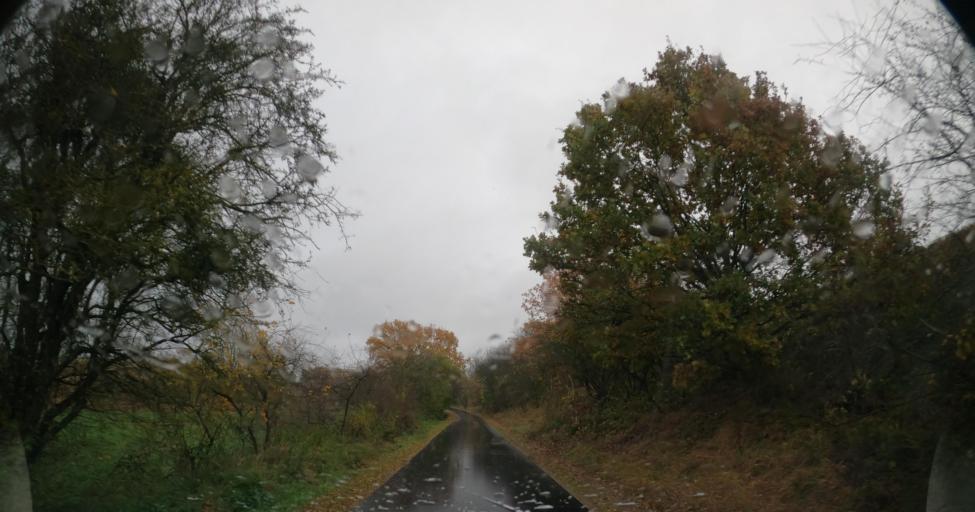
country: PL
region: West Pomeranian Voivodeship
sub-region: Powiat policki
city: Kolbaskowo
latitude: 53.3640
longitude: 14.3643
